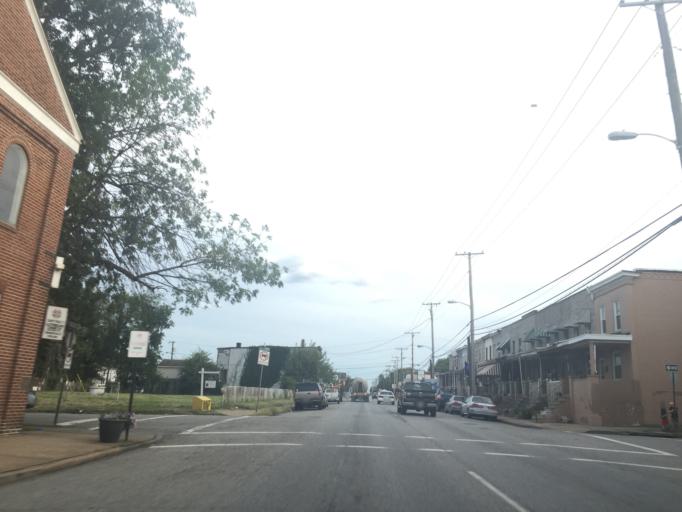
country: US
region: Maryland
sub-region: Anne Arundel County
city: Brooklyn Park
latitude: 39.2293
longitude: -76.5889
